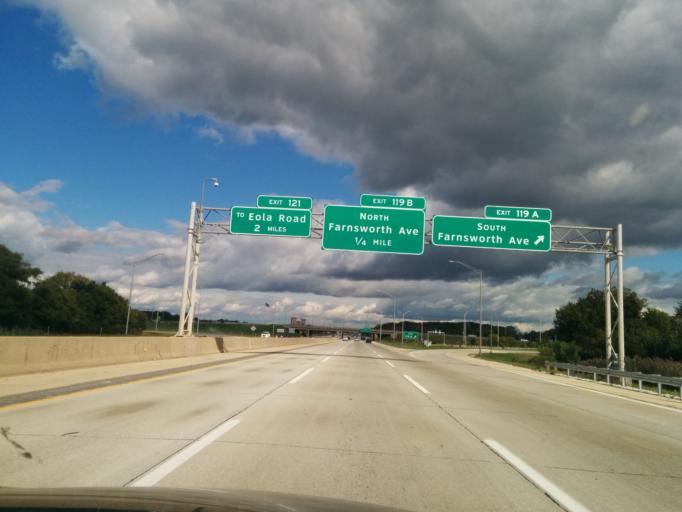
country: US
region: Illinois
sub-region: Kane County
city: North Aurora
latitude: 41.7981
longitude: -88.2870
